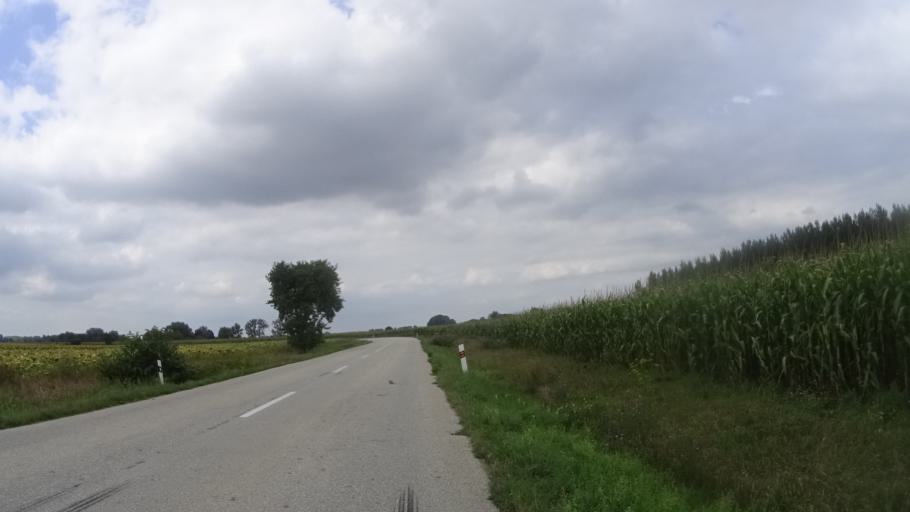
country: HU
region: Gyor-Moson-Sopron
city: Bony
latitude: 47.7590
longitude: 17.8444
